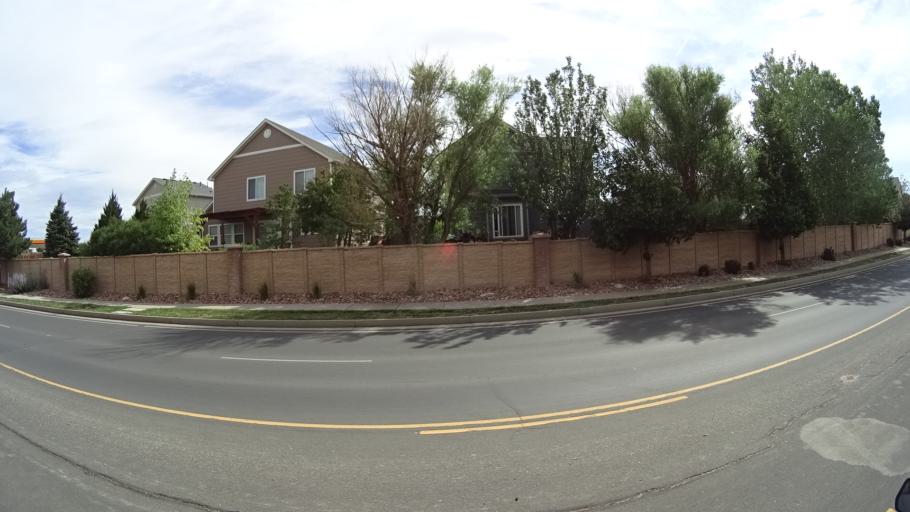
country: US
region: Colorado
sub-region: El Paso County
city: Fountain
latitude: 38.7134
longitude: -104.7011
